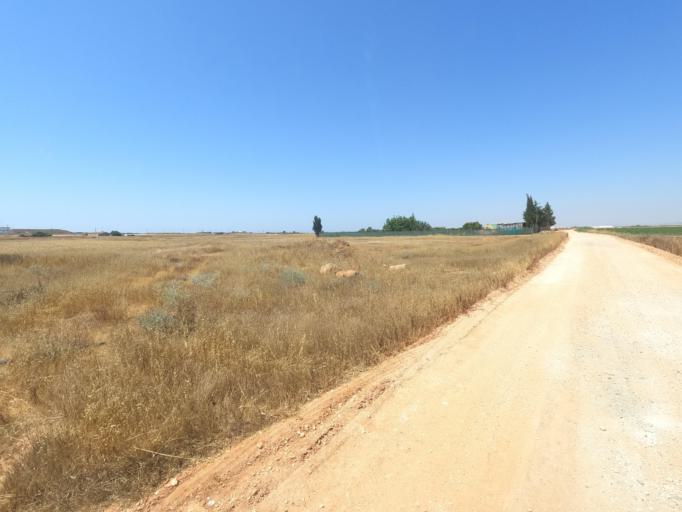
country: CY
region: Ammochostos
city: Liopetri
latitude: 35.0307
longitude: 33.8873
